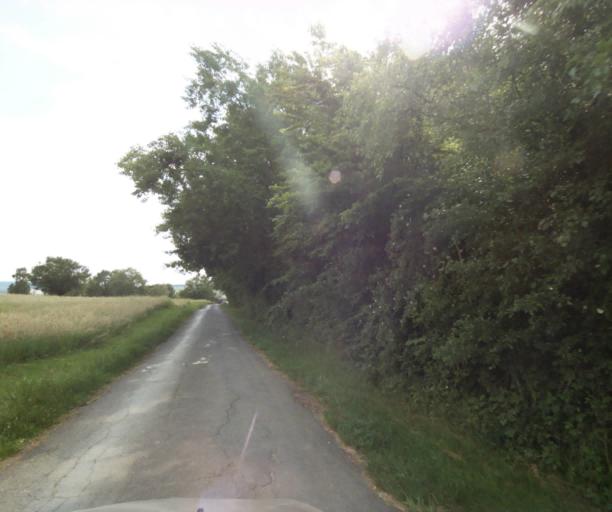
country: FR
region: Champagne-Ardenne
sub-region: Departement des Ardennes
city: Montcy-Notre-Dame
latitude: 49.7642
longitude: 4.7338
